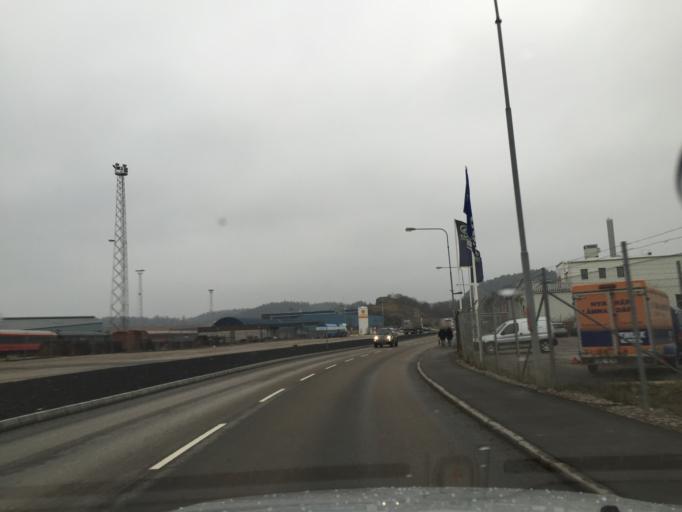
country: SE
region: Vaestra Goetaland
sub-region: Uddevalla Kommun
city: Uddevalla
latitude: 58.3493
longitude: 11.9181
